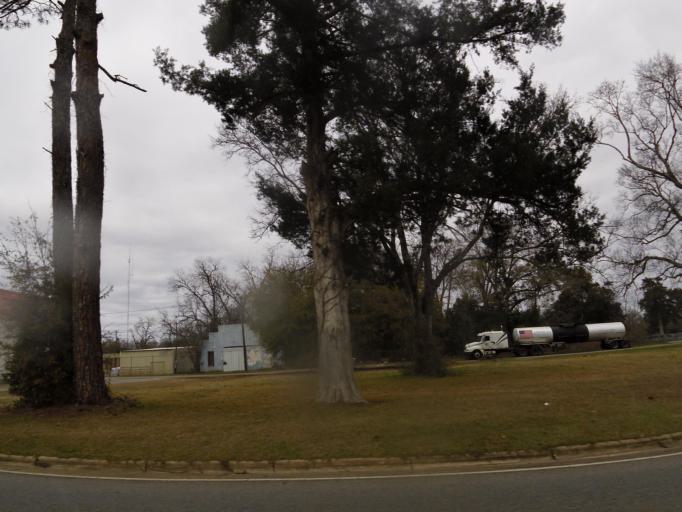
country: US
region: Georgia
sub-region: Randolph County
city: Cuthbert
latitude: 31.7713
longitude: -84.7876
